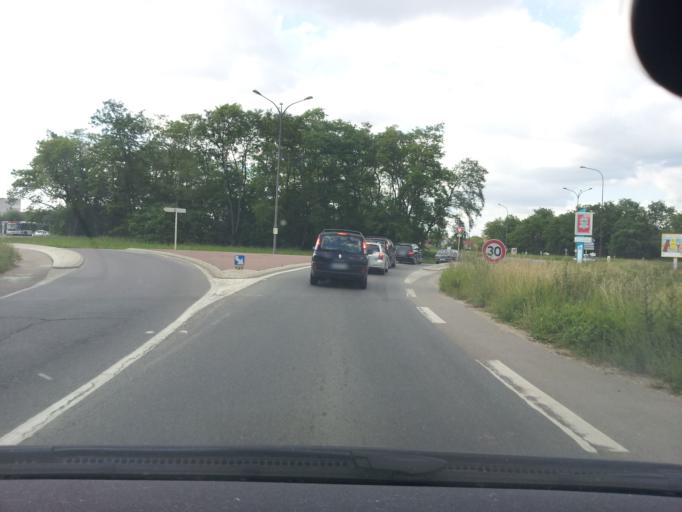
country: FR
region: Ile-de-France
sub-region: Departement de l'Essonne
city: Bondoufle
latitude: 48.6018
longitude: 2.3725
